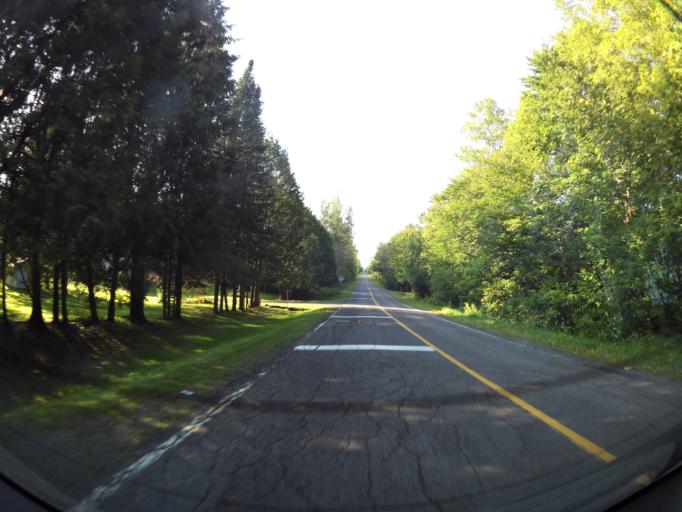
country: CA
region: Ontario
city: Clarence-Rockland
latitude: 45.5038
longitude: -75.4566
